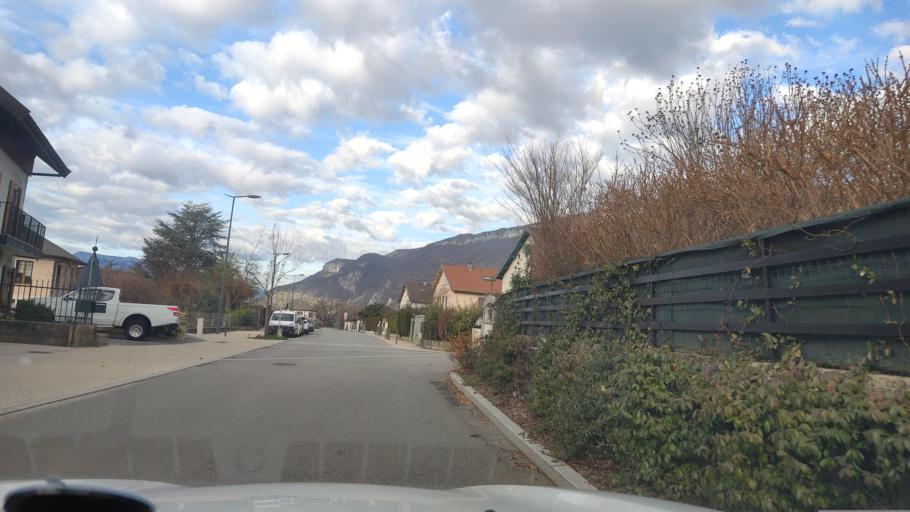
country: FR
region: Rhone-Alpes
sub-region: Departement de la Savoie
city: Brison-Saint-Innocent
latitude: 45.7263
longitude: 5.8879
